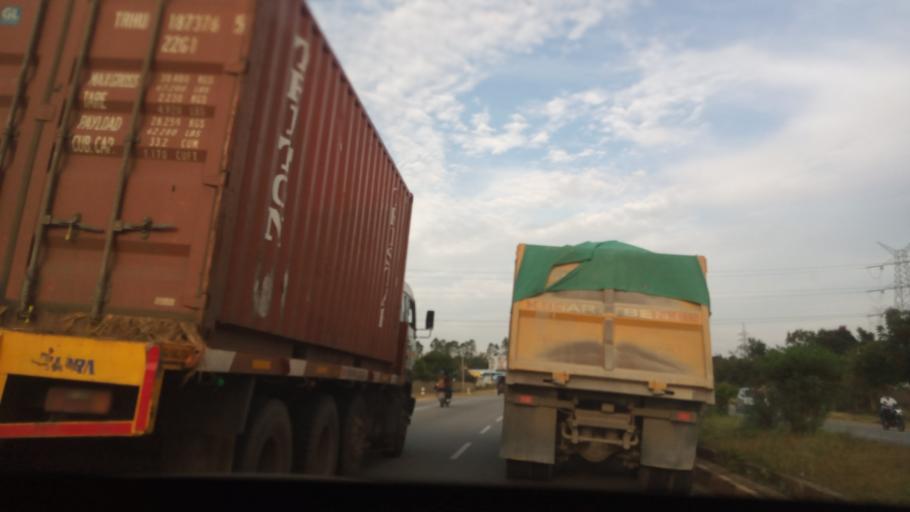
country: IN
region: Karnataka
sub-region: Bangalore Rural
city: Nelamangala
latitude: 13.0807
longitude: 77.3686
